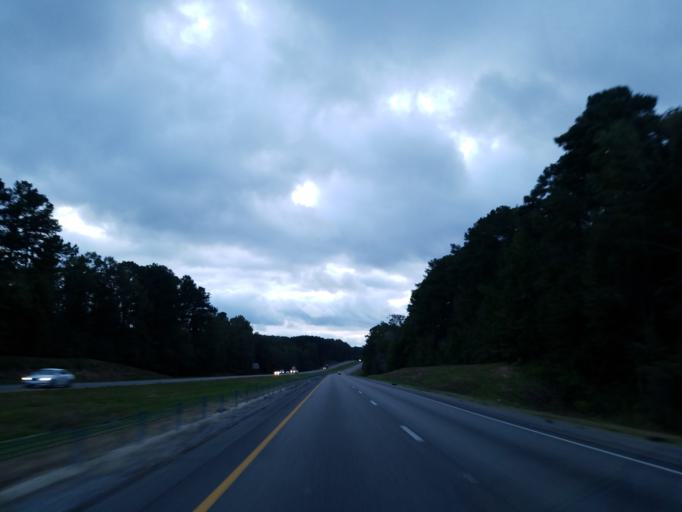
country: US
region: Mississippi
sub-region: Lauderdale County
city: Marion
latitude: 32.3910
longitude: -88.5963
